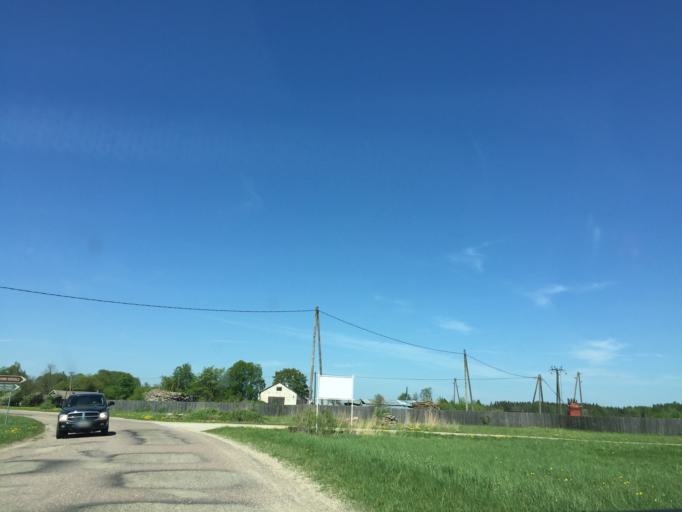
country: LV
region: Ogre
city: Ogre
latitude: 56.8565
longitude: 24.7027
